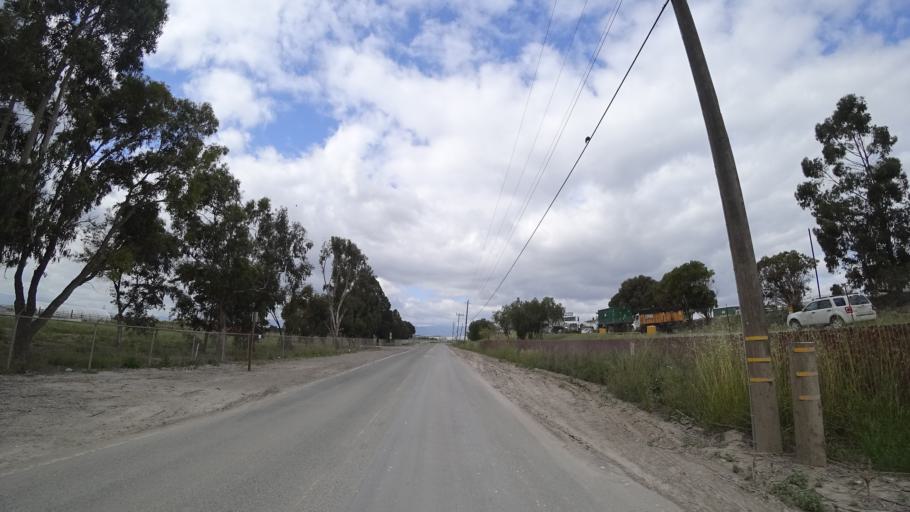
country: US
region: California
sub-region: Santa Clara County
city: Milpitas
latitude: 37.4319
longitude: -121.9538
